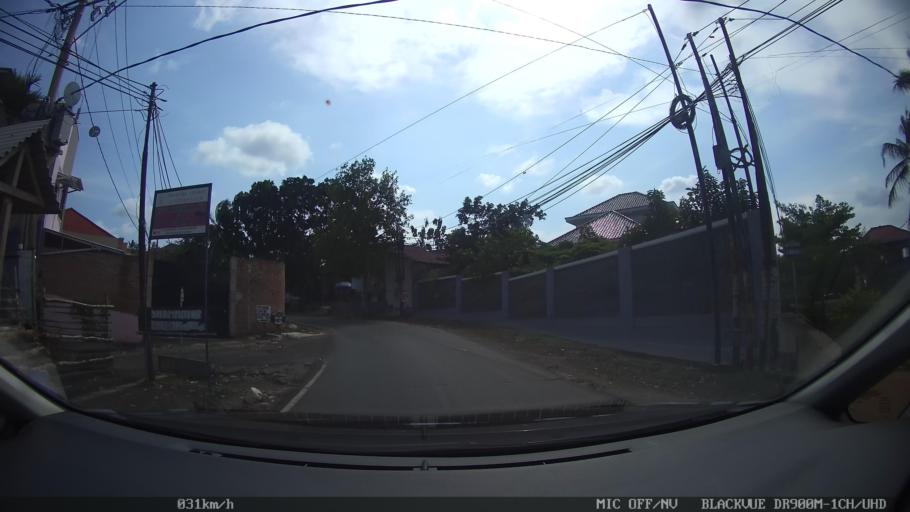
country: ID
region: Lampung
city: Bandarlampung
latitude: -5.4040
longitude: 105.2308
